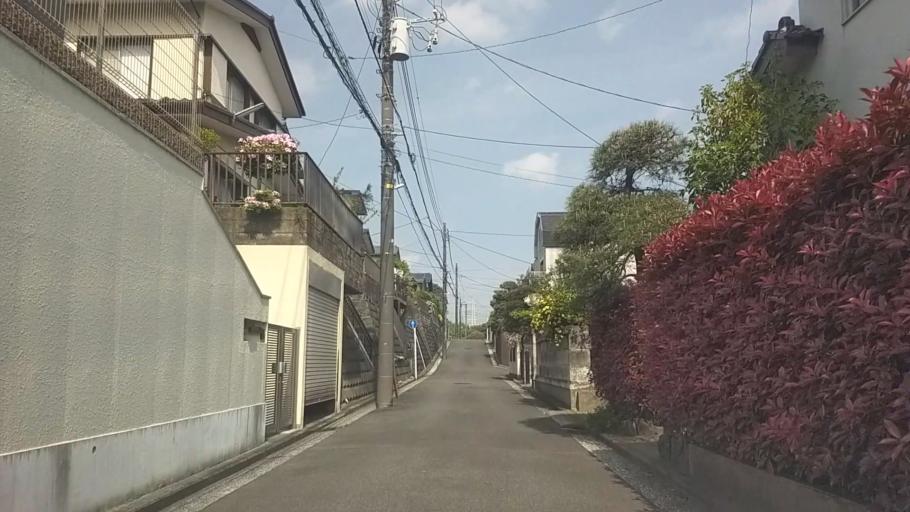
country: JP
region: Kanagawa
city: Yokohama
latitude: 35.3737
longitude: 139.6158
